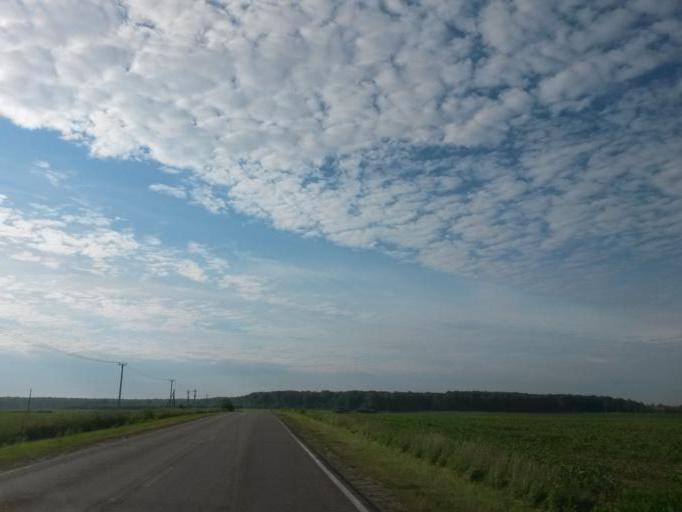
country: RU
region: Moskovskaya
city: Melikhovo
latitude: 55.1956
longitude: 37.6942
